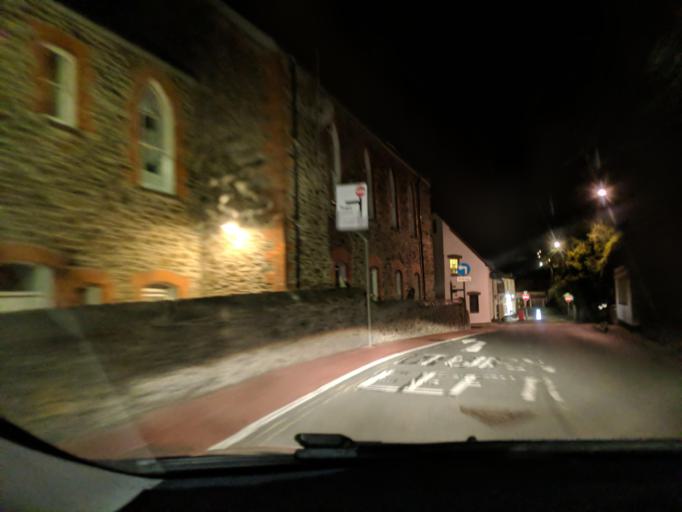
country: GB
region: England
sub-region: Cornwall
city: Mevagissey
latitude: 50.2711
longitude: -4.7895
